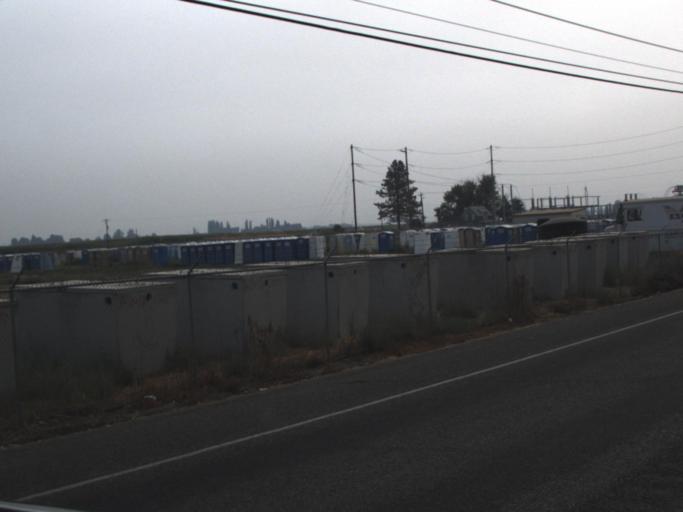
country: US
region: Washington
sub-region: Yakima County
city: Sunnyside
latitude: 46.2967
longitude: -119.9992
